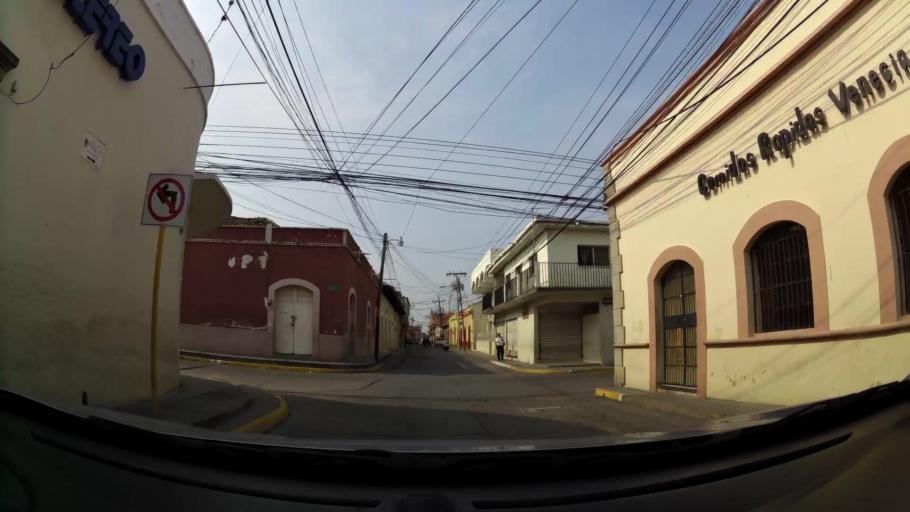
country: HN
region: Comayagua
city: Comayagua
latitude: 14.4590
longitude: -87.6418
